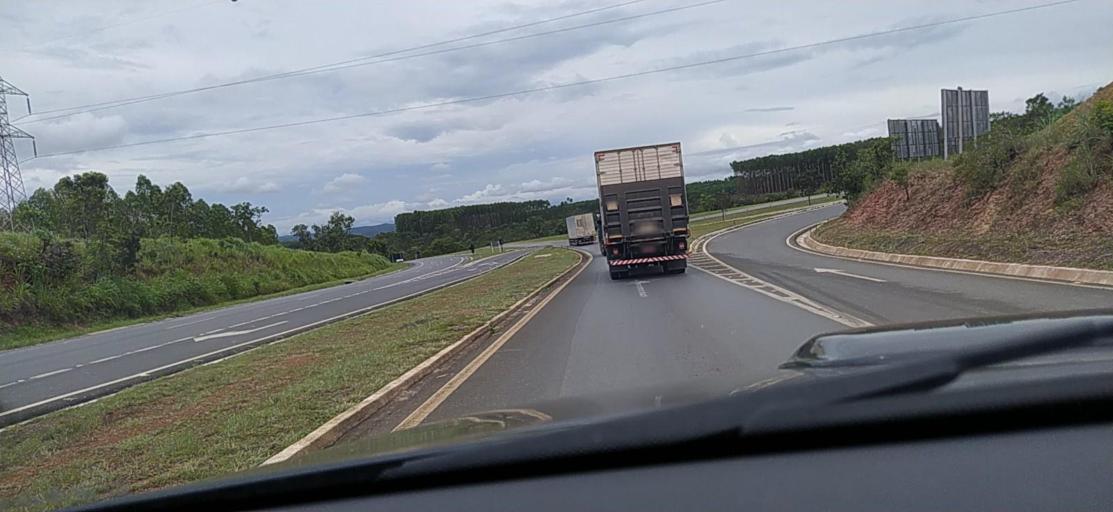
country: BR
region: Minas Gerais
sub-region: Curvelo
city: Curvelo
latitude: -18.7060
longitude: -44.4408
